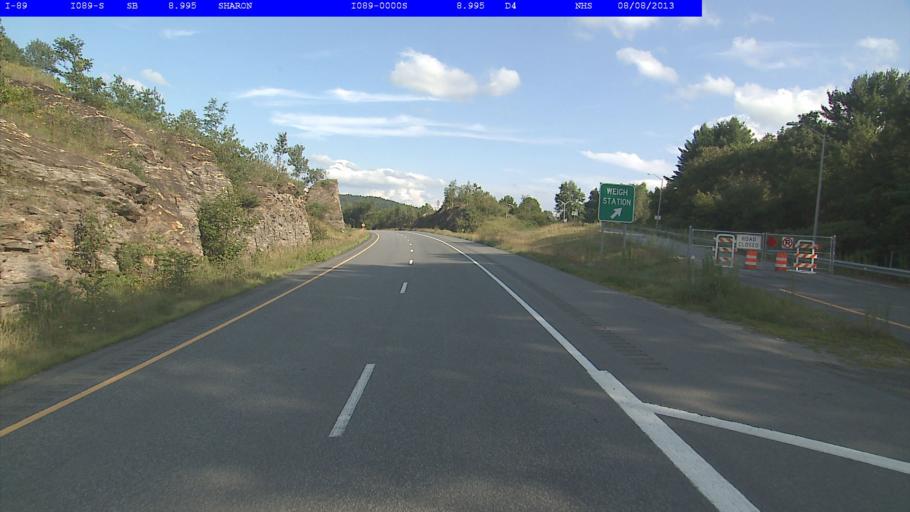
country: US
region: Vermont
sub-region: Windsor County
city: Wilder
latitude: 43.7282
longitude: -72.4300
